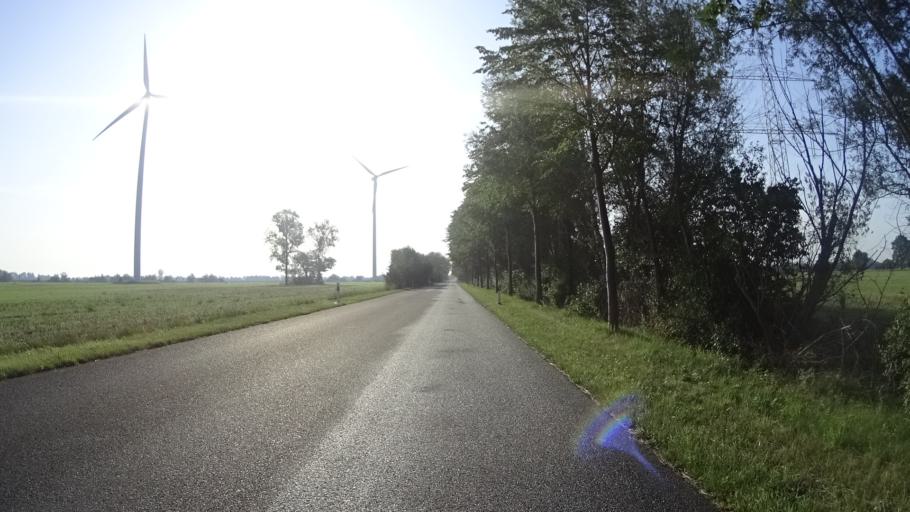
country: DE
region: Brandenburg
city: Kasel-Golzig
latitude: 51.9824
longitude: 13.7280
